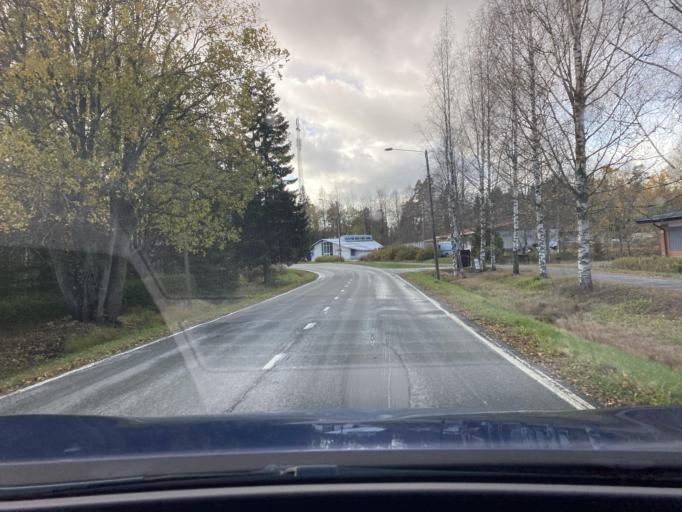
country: FI
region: Varsinais-Suomi
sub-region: Loimaa
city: Aura
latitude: 60.7175
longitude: 22.6018
